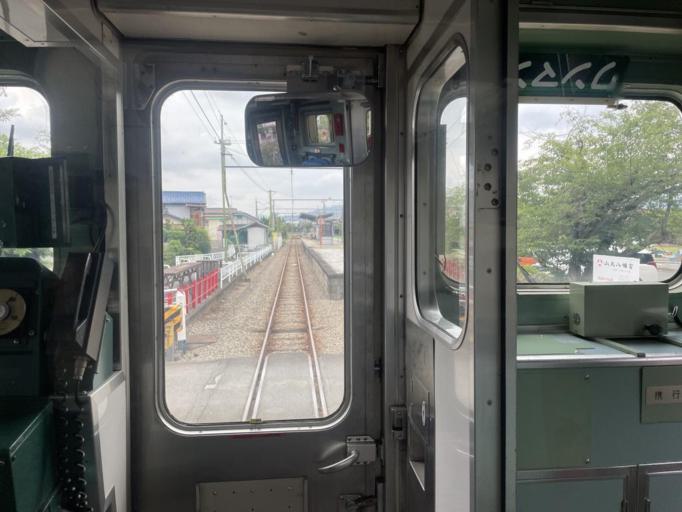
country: JP
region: Gunma
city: Fujioka
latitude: 36.2784
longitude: 139.0381
